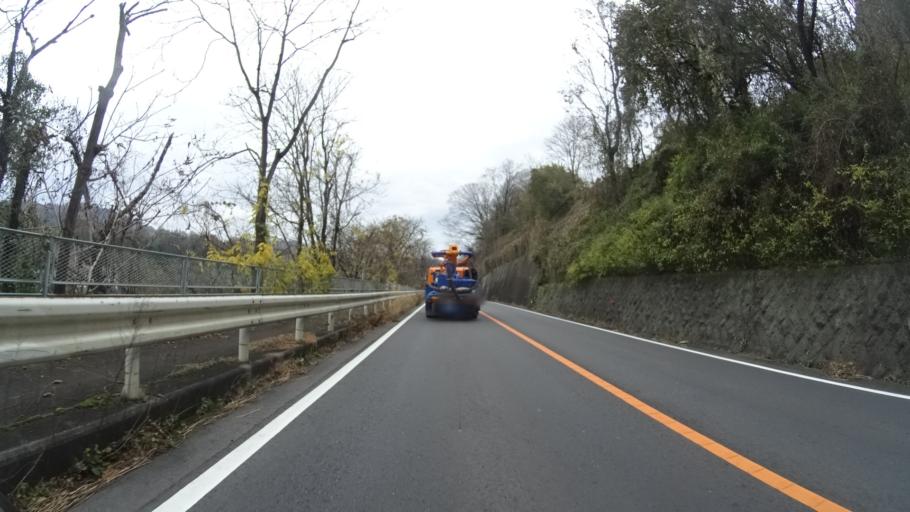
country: JP
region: Gunma
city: Numata
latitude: 36.6085
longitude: 139.0430
